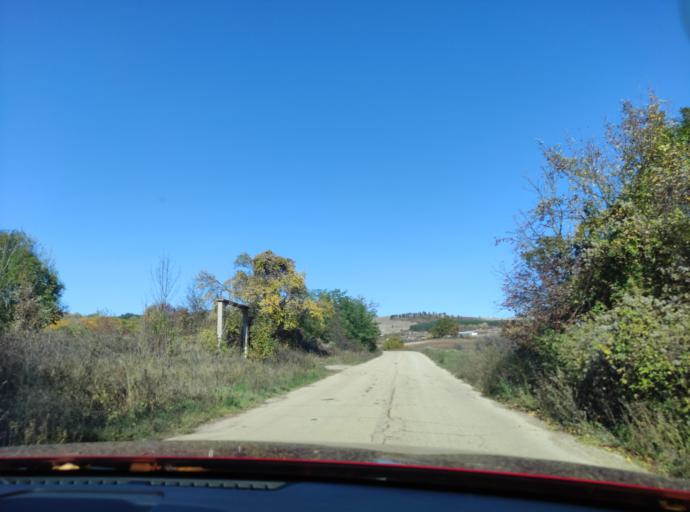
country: BG
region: Montana
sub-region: Obshtina Montana
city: Montana
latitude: 43.4255
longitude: 23.0649
